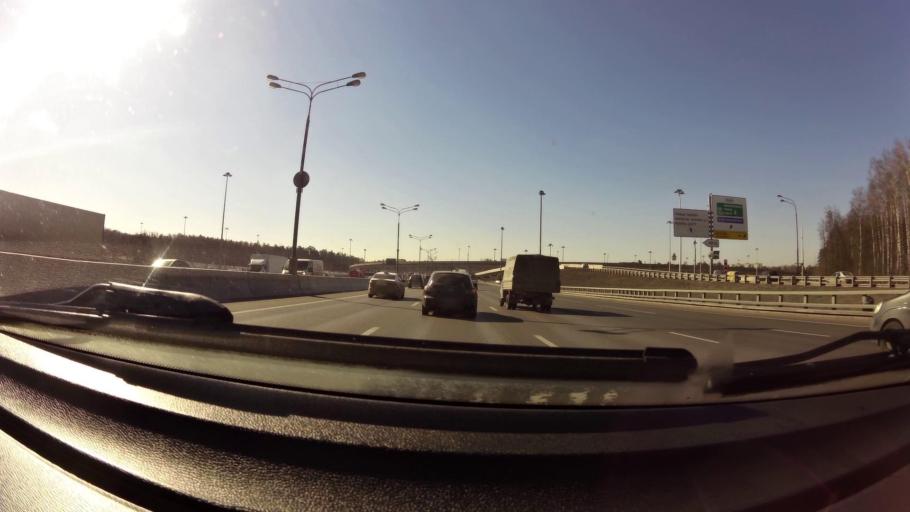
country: RU
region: Moscow
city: Rublevo
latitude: 55.7918
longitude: 37.3746
